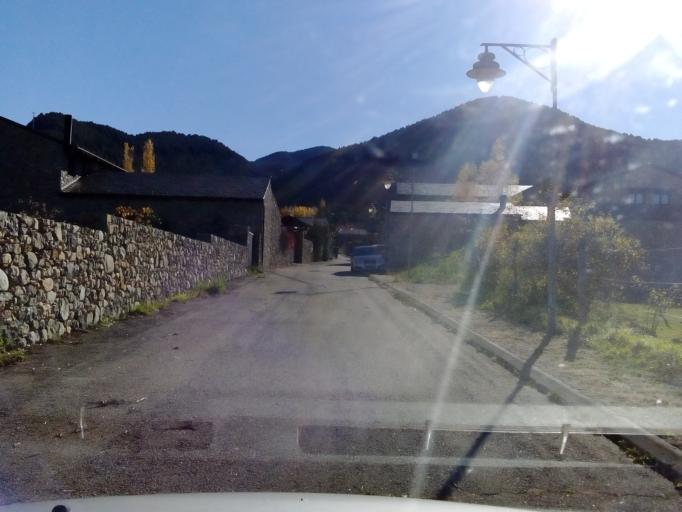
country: ES
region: Catalonia
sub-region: Provincia de Lleida
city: Bellver de Cerdanya
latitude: 42.3431
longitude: 1.7752
